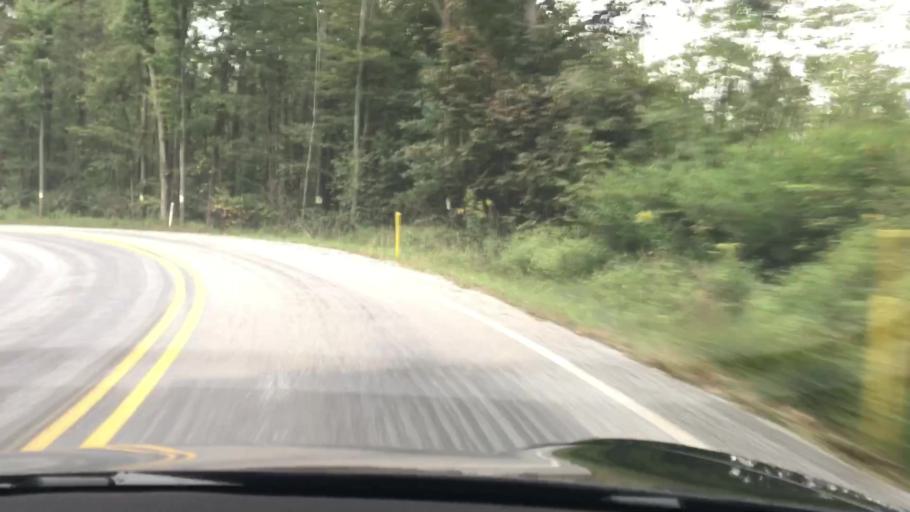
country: US
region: Pennsylvania
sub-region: York County
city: Dillsburg
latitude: 40.0599
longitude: -77.0738
